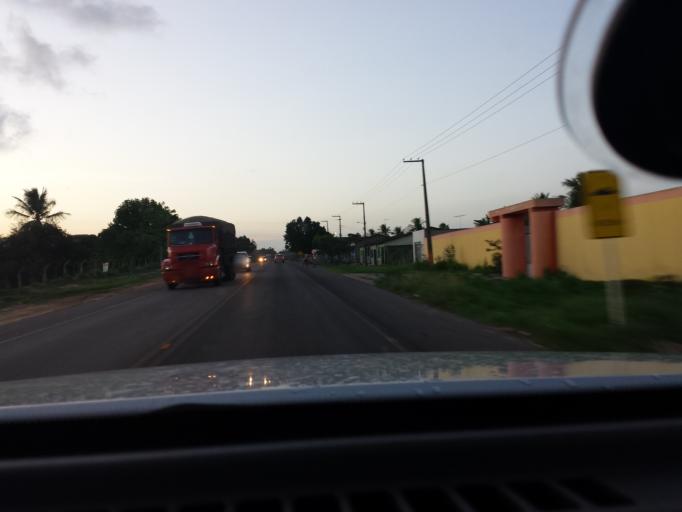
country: BR
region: Sergipe
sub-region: Salgado
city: Salgado
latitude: -11.0013
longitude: -37.5197
